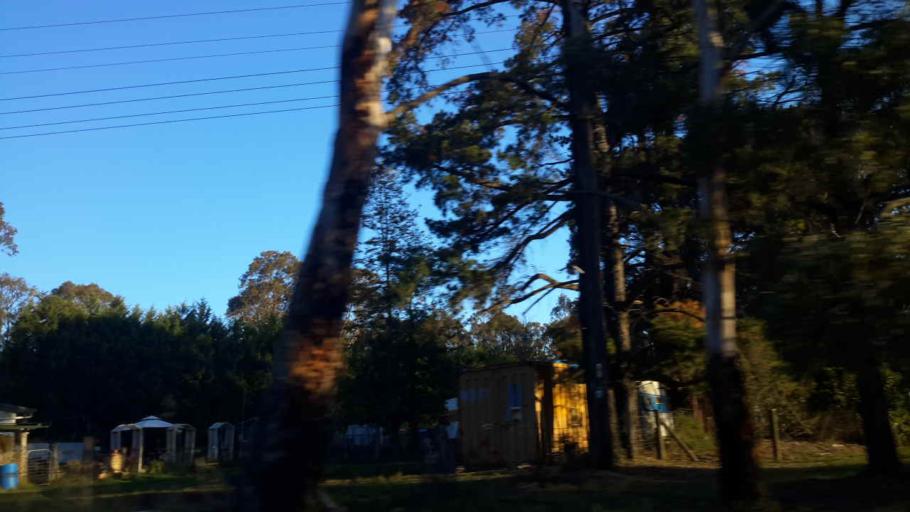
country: AU
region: New South Wales
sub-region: Wollondilly
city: Douglas Park
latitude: -34.2405
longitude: 150.7178
